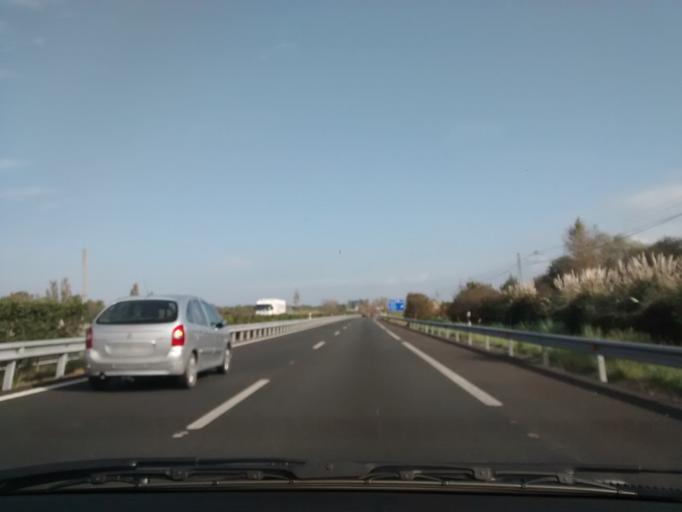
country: ES
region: Cantabria
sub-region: Provincia de Cantabria
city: El Astillero
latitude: 43.3991
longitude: -3.7814
